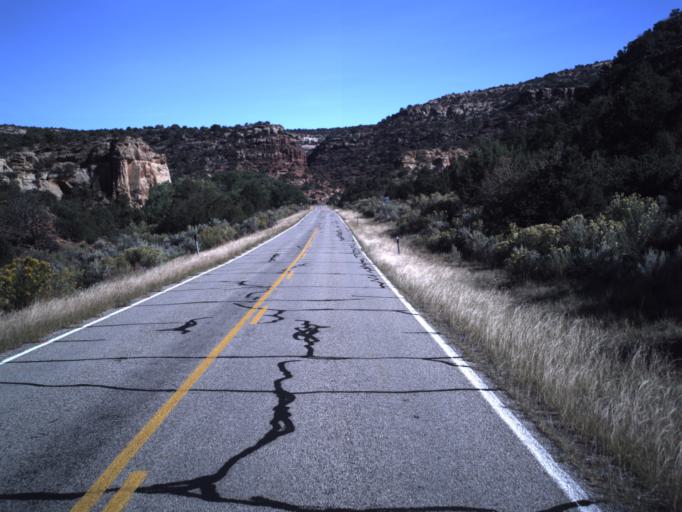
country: US
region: Utah
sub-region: San Juan County
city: Monticello
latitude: 37.9855
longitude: -109.5092
